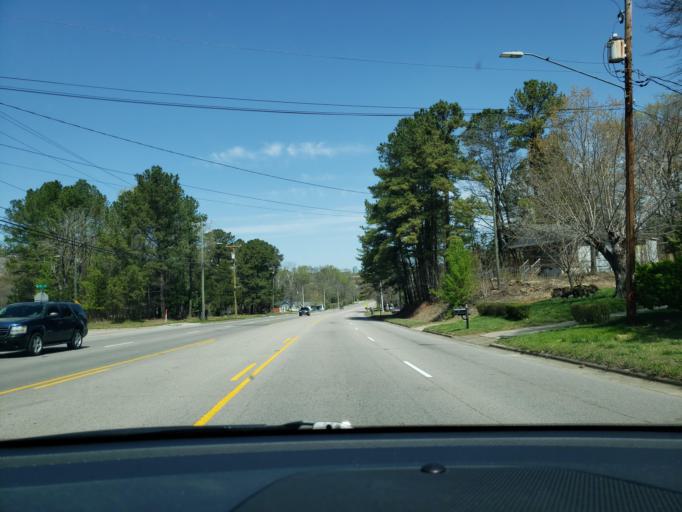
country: US
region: North Carolina
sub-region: Durham County
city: Durham
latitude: 35.9638
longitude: -78.8949
